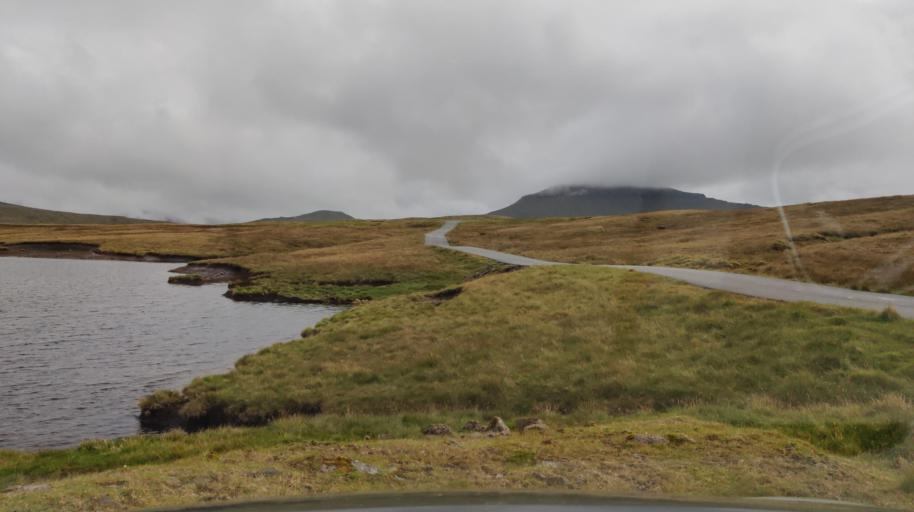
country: FO
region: Streymoy
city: Vestmanna
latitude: 62.1646
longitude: -7.0912
